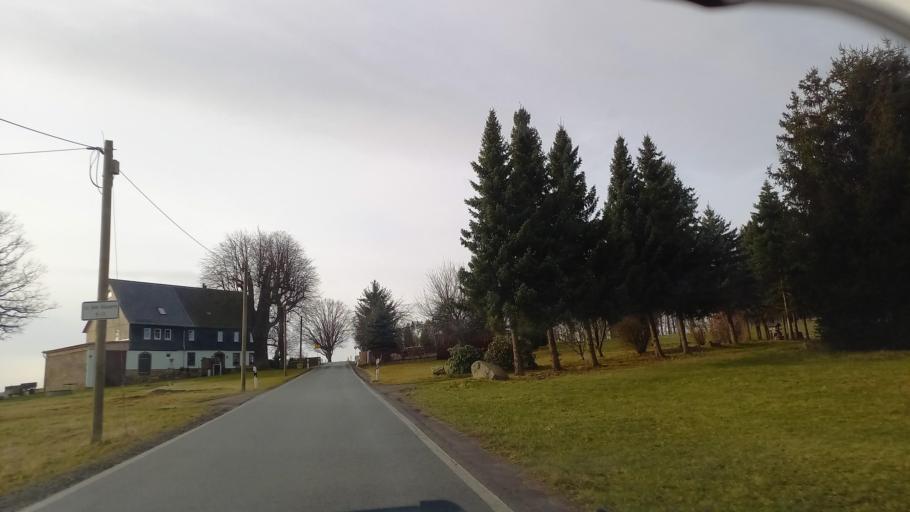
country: DE
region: Saxony
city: Kirchberg
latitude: 50.6121
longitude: 12.5130
